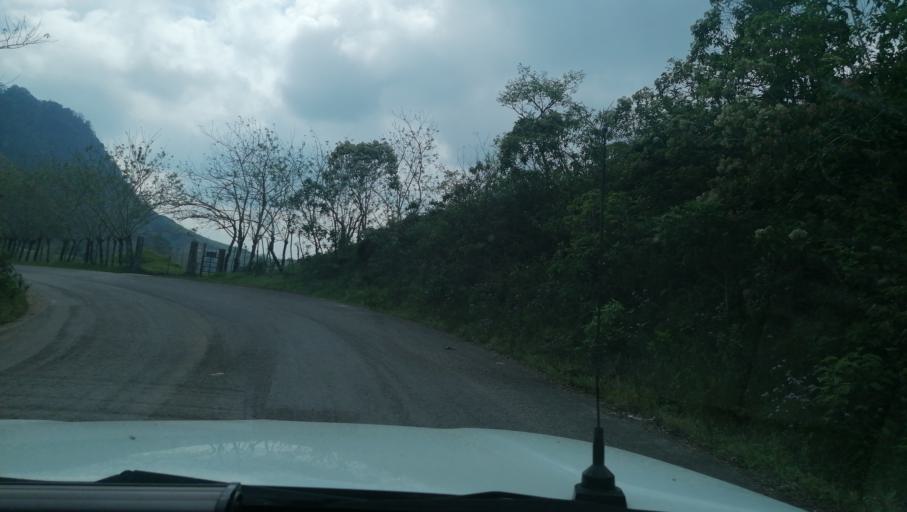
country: MX
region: Chiapas
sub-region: Francisco Leon
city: San Miguel la Sardina
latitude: 17.2510
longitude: -93.2818
